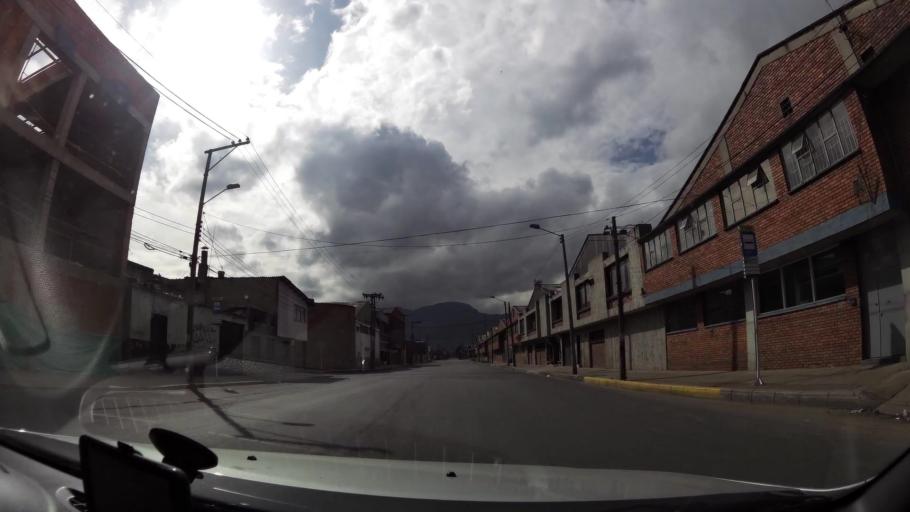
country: CO
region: Bogota D.C.
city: Bogota
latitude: 4.6213
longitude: -74.1035
